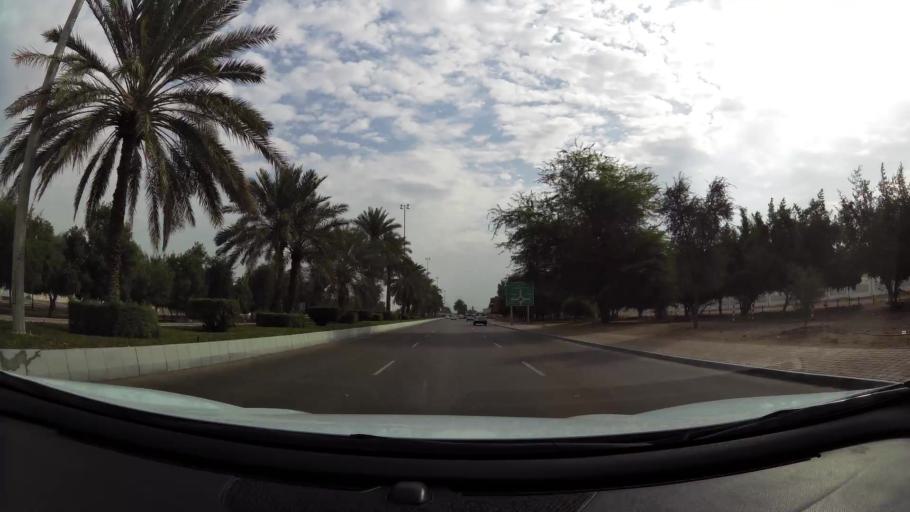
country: AE
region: Abu Dhabi
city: Al Ain
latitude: 24.2067
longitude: 55.6845
